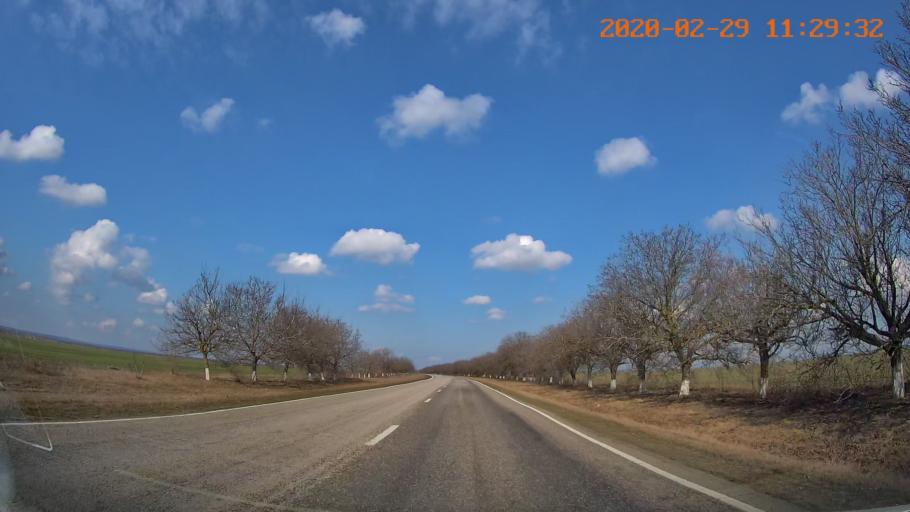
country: MD
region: Telenesti
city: Cocieri
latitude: 47.4960
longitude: 29.1247
